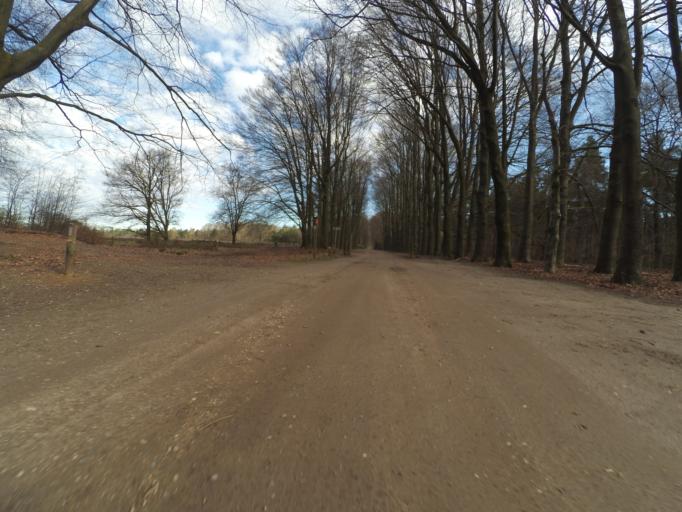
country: NL
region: Gelderland
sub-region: Gemeente Apeldoorn
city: Uddel
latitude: 52.1819
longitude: 5.8458
